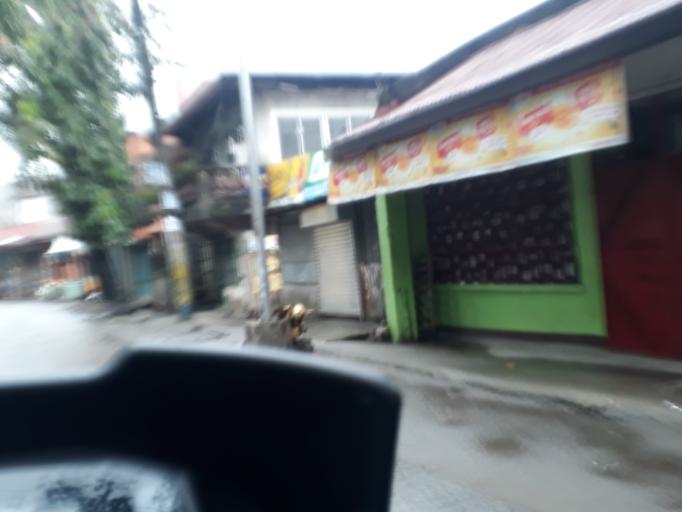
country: PH
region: Central Luzon
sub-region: Province of Bulacan
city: San Jose del Monte
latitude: 14.7705
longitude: 121.0529
